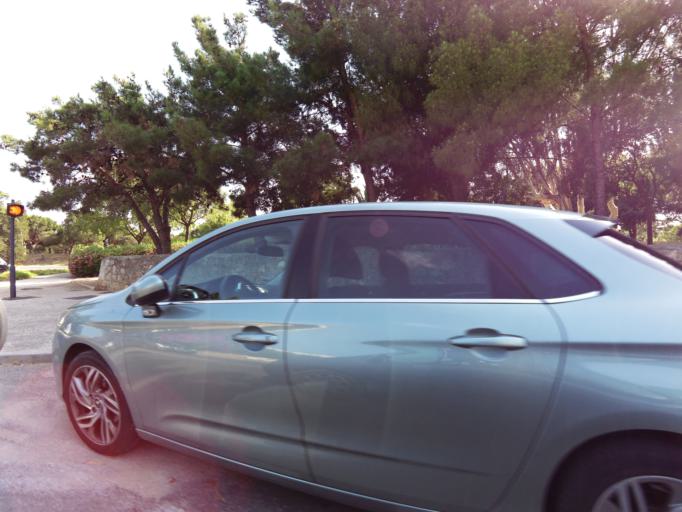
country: FR
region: Provence-Alpes-Cote d'Azur
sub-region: Departement du Var
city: Hyeres
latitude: 43.1179
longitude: 6.1441
